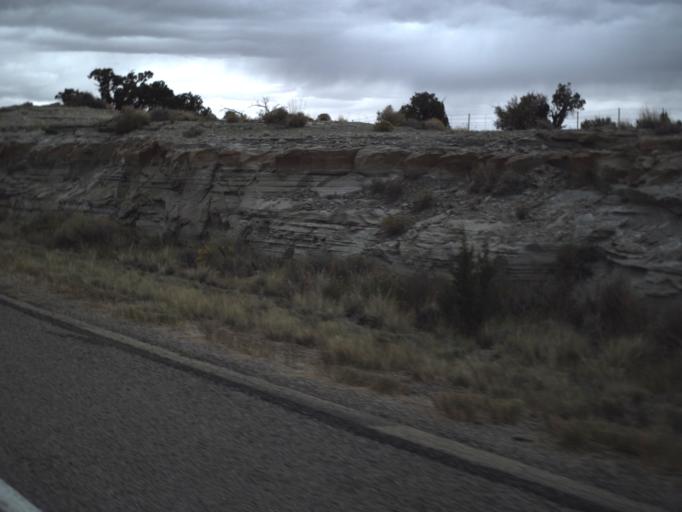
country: US
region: Utah
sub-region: Emery County
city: Ferron
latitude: 38.8307
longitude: -111.1230
